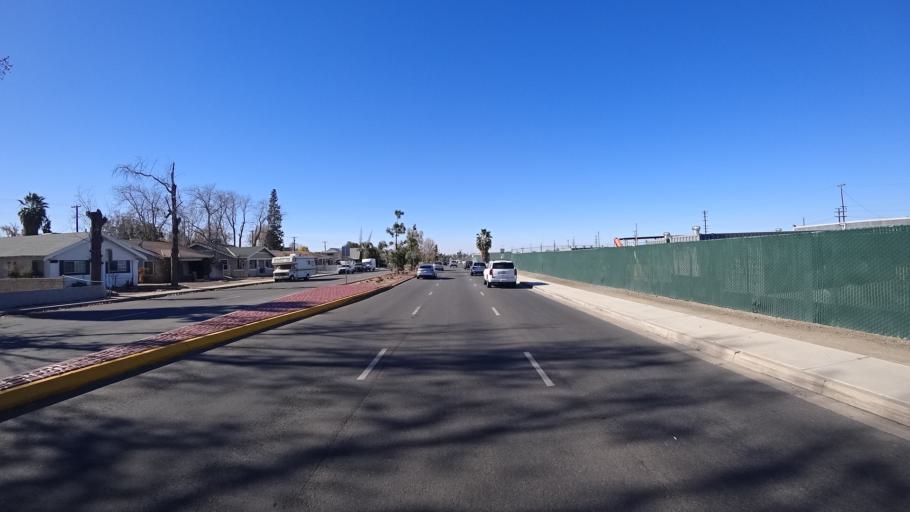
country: US
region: California
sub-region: Kern County
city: Bakersfield
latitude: 35.3685
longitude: -119.0299
